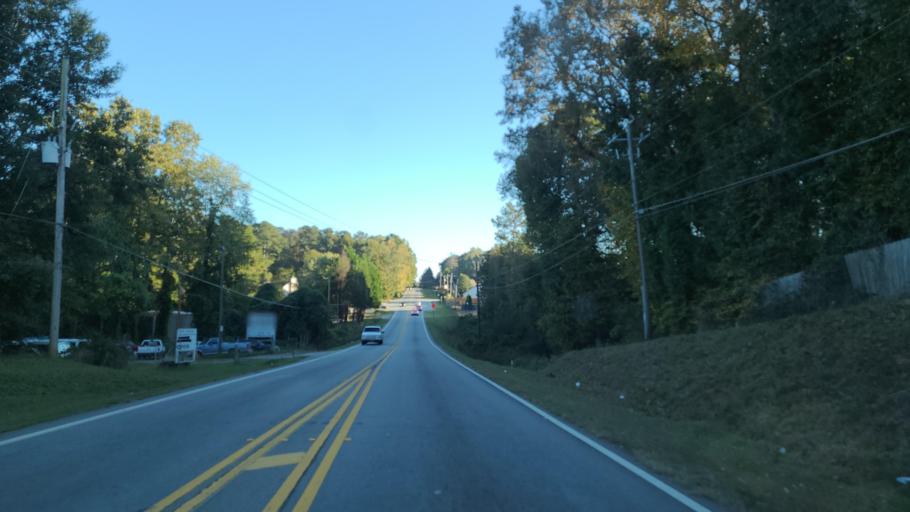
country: US
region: Georgia
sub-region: Clayton County
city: Lake City
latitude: 33.5998
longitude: -84.2983
